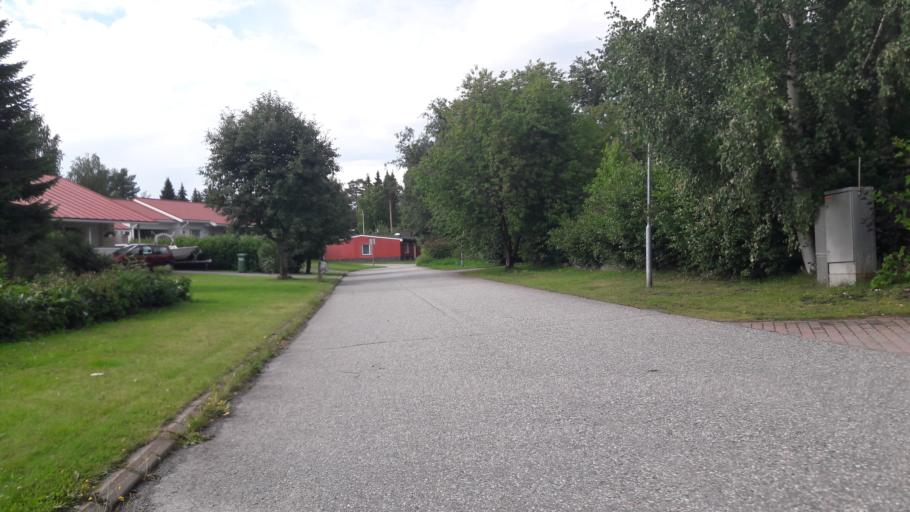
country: FI
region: North Karelia
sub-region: Joensuu
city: Joensuu
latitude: 62.5841
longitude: 29.8070
